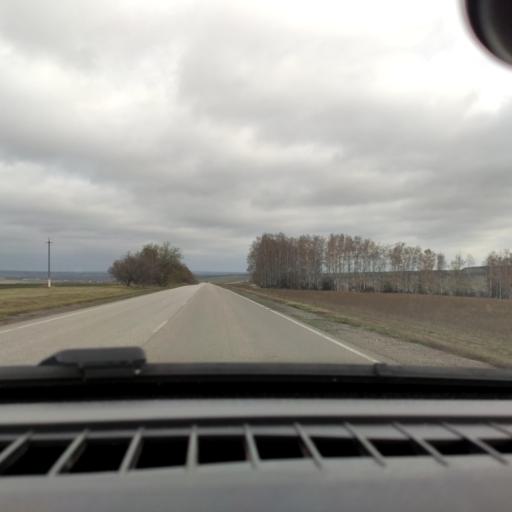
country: RU
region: Belgorod
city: Ilovka
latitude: 50.7607
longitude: 38.7376
